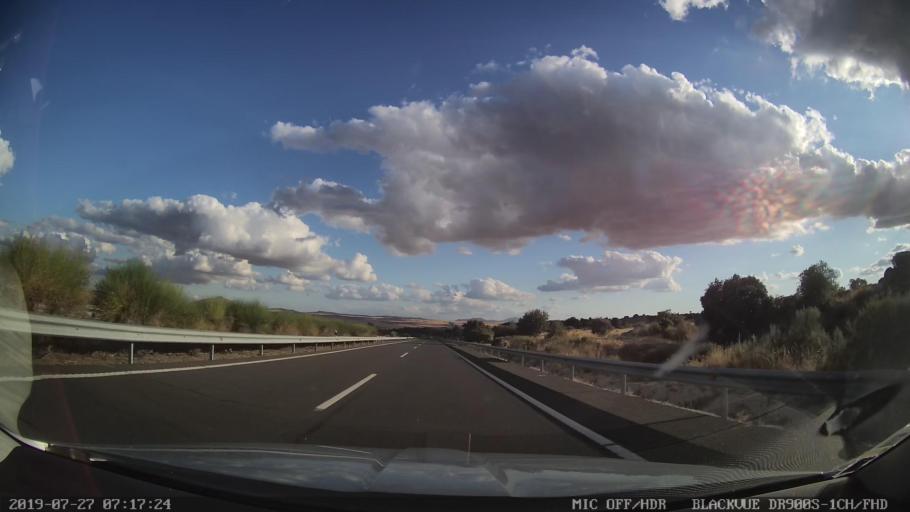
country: ES
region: Extremadura
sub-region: Provincia de Caceres
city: Trujillo
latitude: 39.4402
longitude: -5.8767
